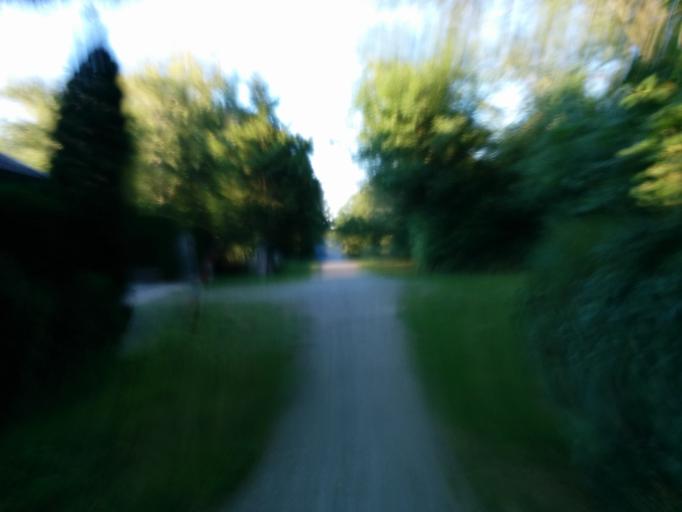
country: AT
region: Lower Austria
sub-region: Politischer Bezirk Modling
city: Munchendorf
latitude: 48.0231
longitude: 16.3748
